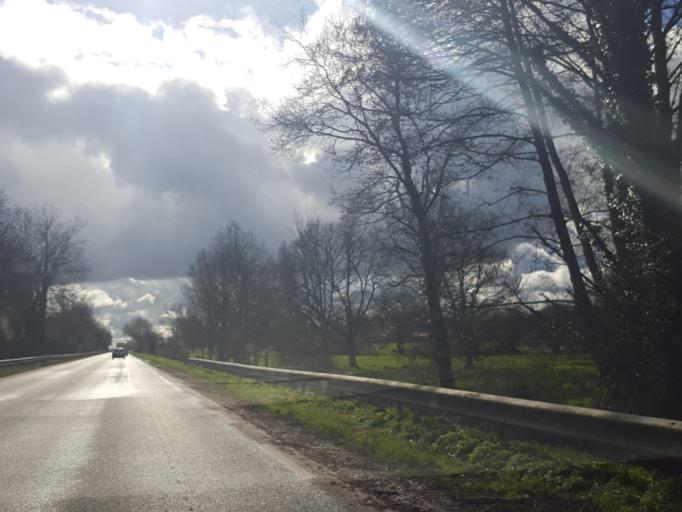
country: FR
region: Pays de la Loire
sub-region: Departement de la Vendee
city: Belleville-sur-Vie
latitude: 46.7629
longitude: -1.4310
